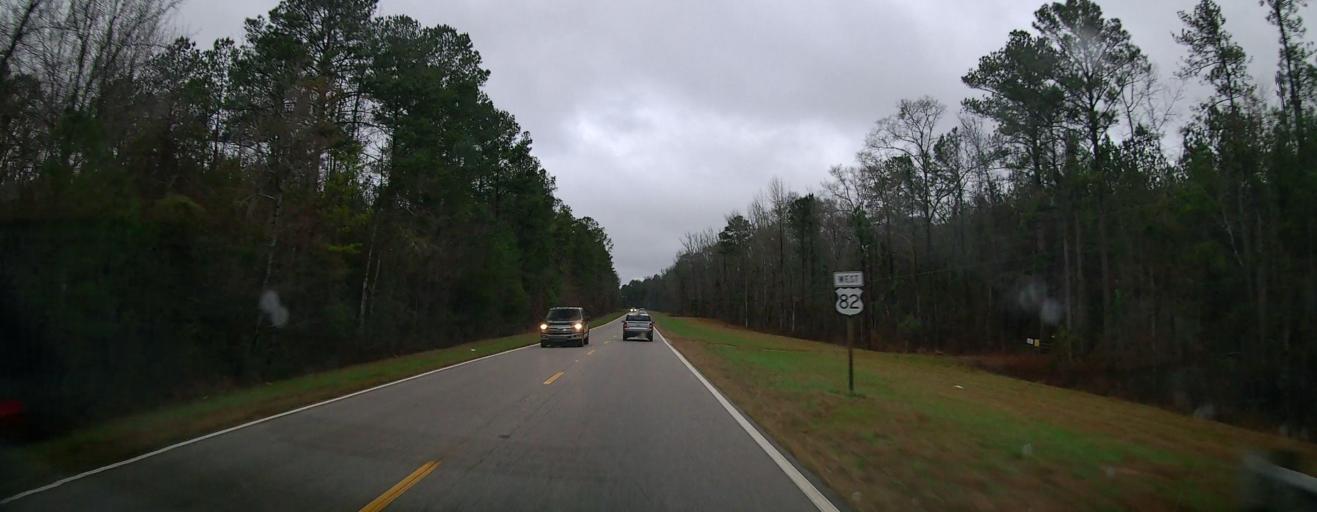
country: US
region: Alabama
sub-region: Bibb County
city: Centreville
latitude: 32.8913
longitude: -86.9864
